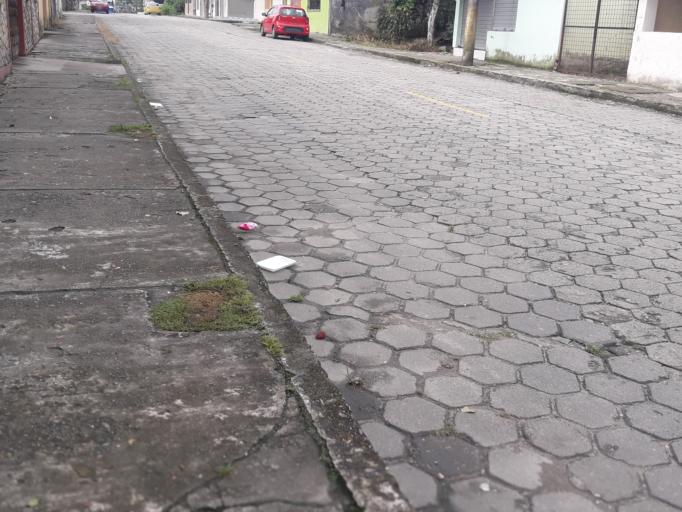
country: EC
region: Napo
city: Tena
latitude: -0.9968
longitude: -77.8148
